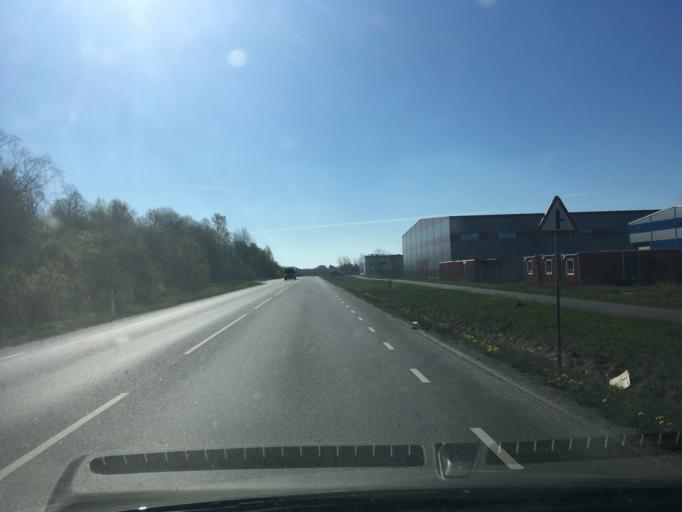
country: EE
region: Harju
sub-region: Tallinna linn
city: Kose
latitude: 59.4144
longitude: 24.8994
